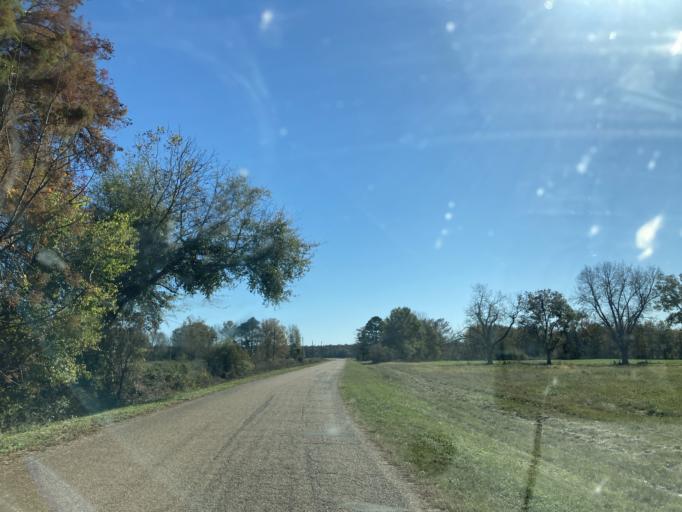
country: US
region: Mississippi
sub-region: Hinds County
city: Lynchburg
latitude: 32.6374
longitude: -90.6054
